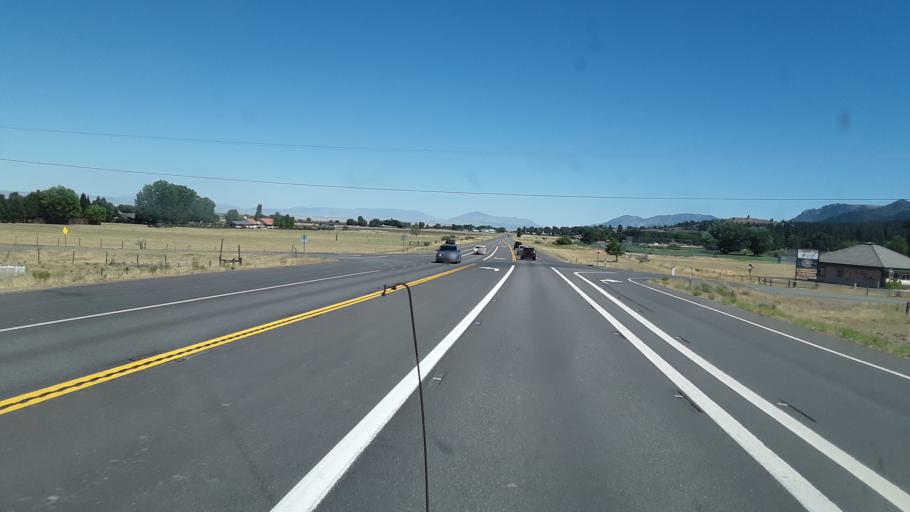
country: US
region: California
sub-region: Lassen County
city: Janesville
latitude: 40.3034
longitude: -120.5249
